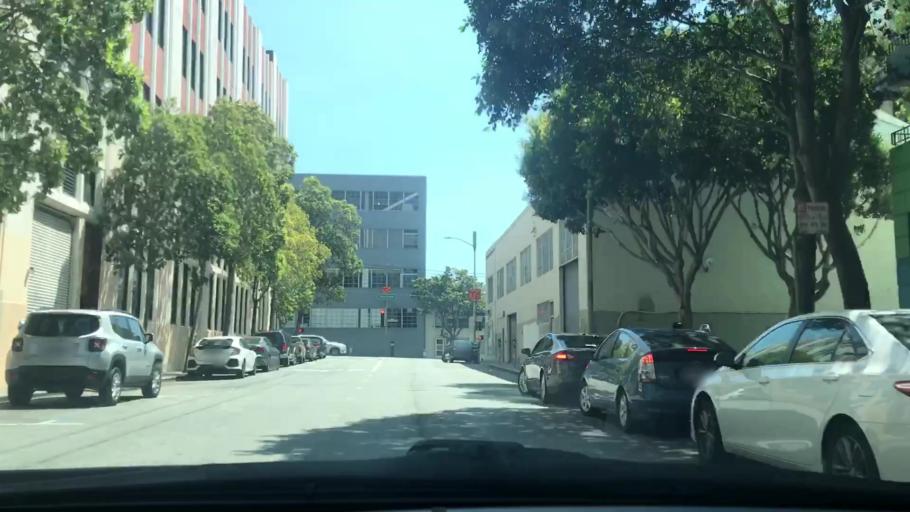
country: US
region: California
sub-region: San Francisco County
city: San Francisco
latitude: 37.7839
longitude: -122.3970
